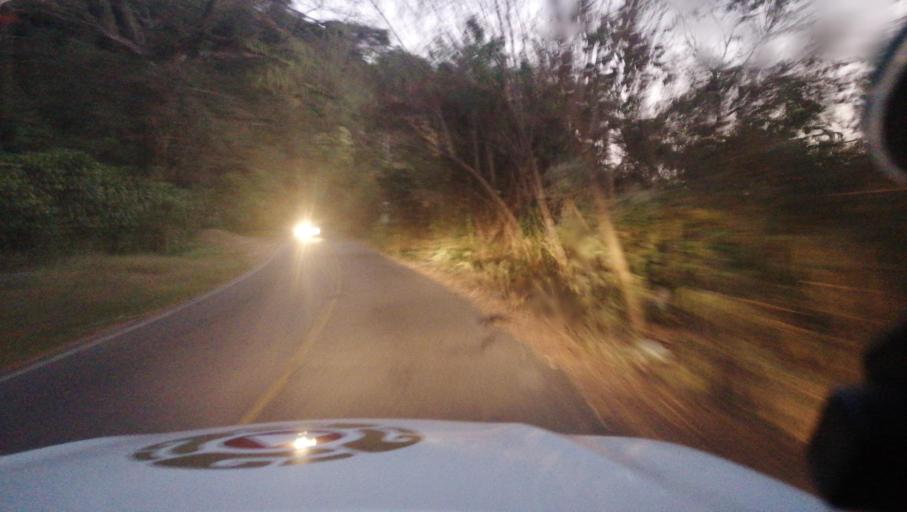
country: MX
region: Chiapas
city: Veinte de Noviembre
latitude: 14.9712
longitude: -92.2522
